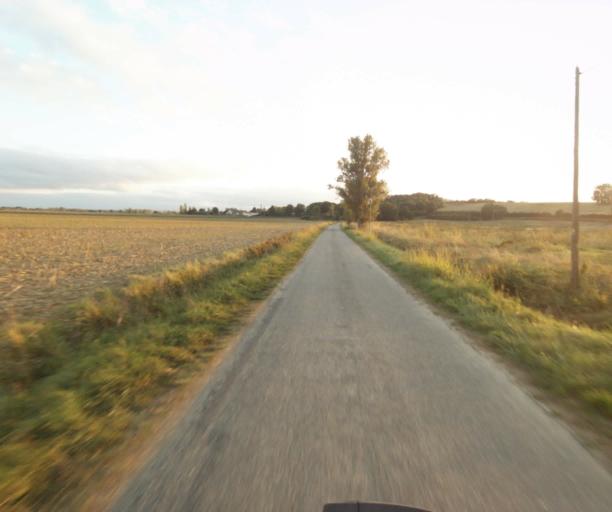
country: FR
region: Midi-Pyrenees
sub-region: Departement du Tarn-et-Garonne
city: Verdun-sur-Garonne
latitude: 43.8281
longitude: 1.2122
